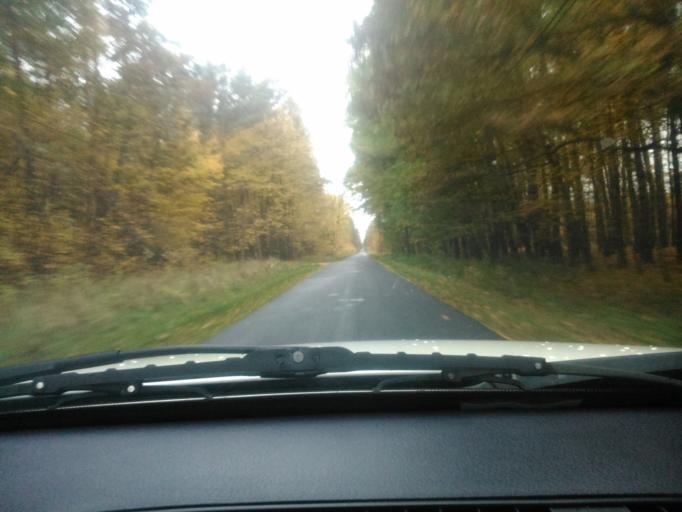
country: PL
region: Kujawsko-Pomorskie
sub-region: Powiat golubsko-dobrzynski
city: Golub-Dobrzyn
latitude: 53.1457
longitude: 19.1293
